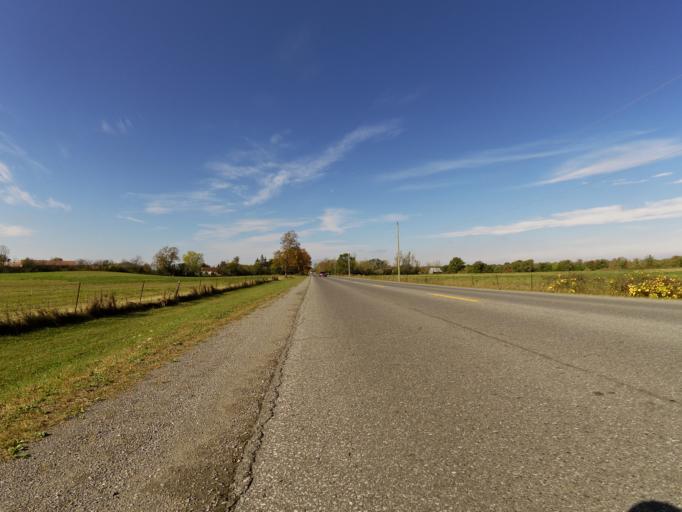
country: CA
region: Ontario
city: Prince Edward
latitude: 44.0150
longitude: -77.3122
